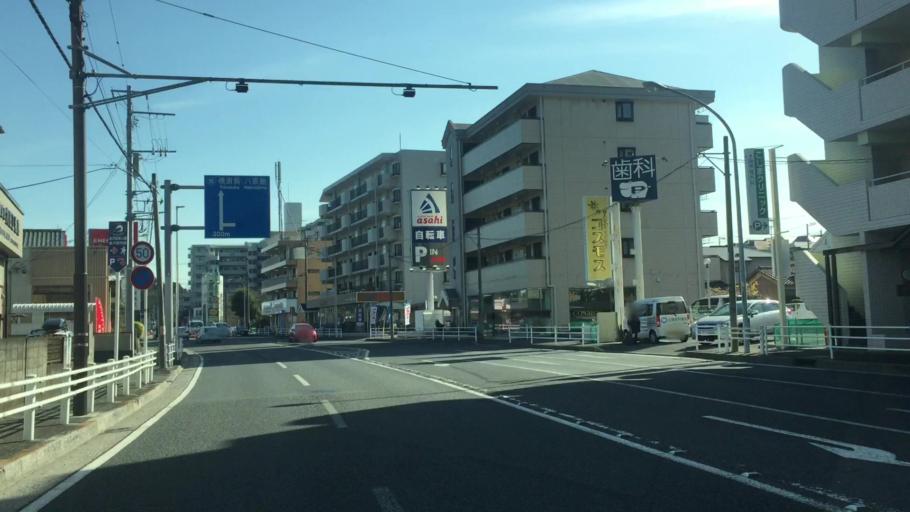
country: JP
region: Kanagawa
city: Zushi
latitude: 35.3470
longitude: 139.6086
